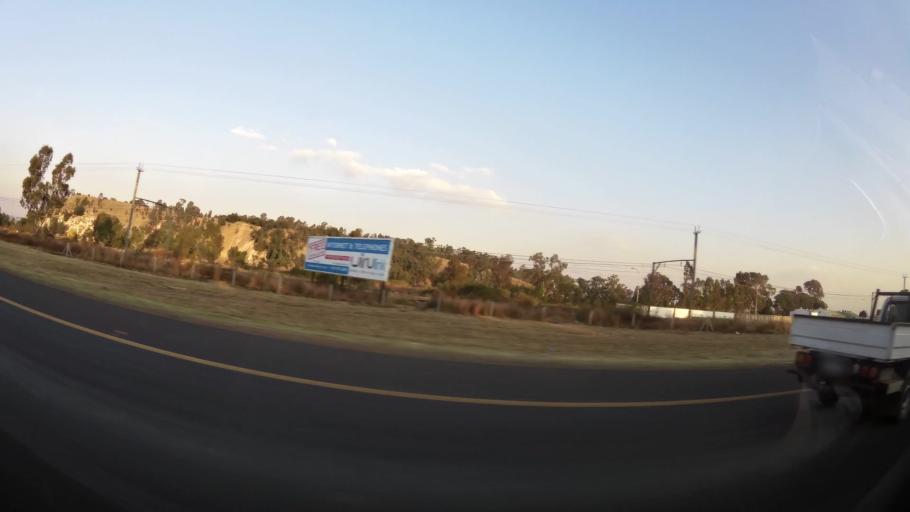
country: ZA
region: Gauteng
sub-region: Ekurhuleni Metropolitan Municipality
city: Benoni
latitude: -26.1691
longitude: 28.3522
